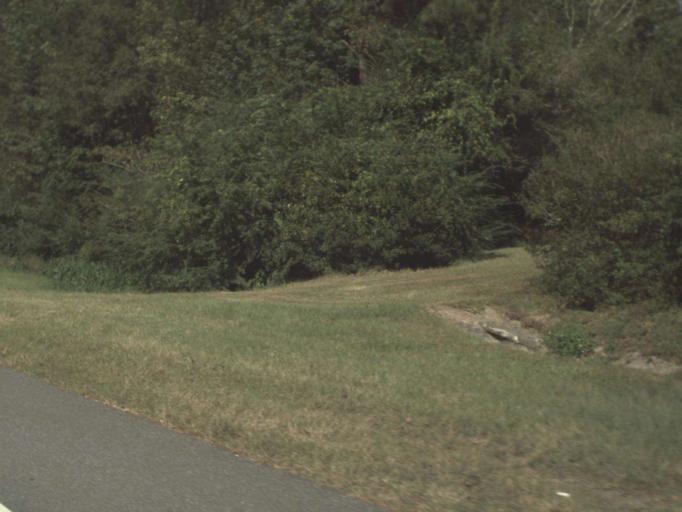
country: US
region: Alabama
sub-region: Covington County
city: Florala
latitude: 30.9645
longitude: -86.4426
